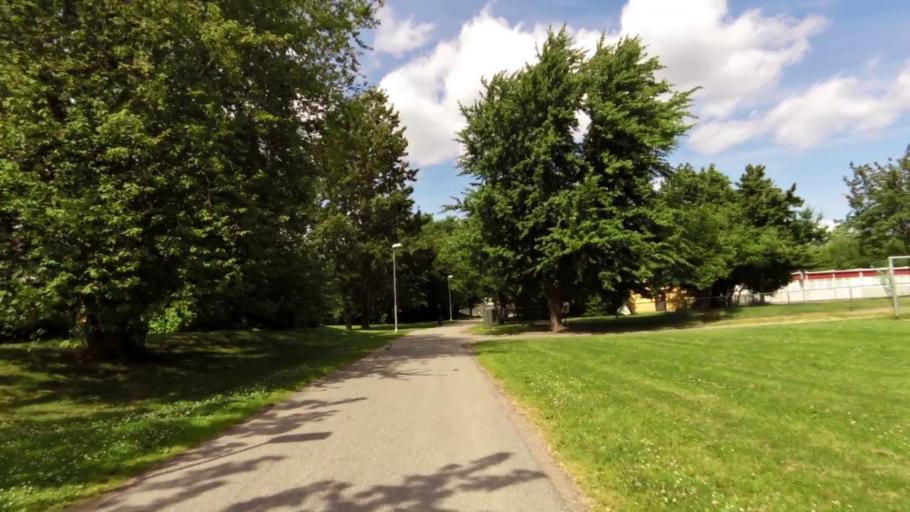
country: SE
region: OEstergoetland
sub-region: Linkopings Kommun
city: Linkoping
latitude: 58.4236
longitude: 15.5843
